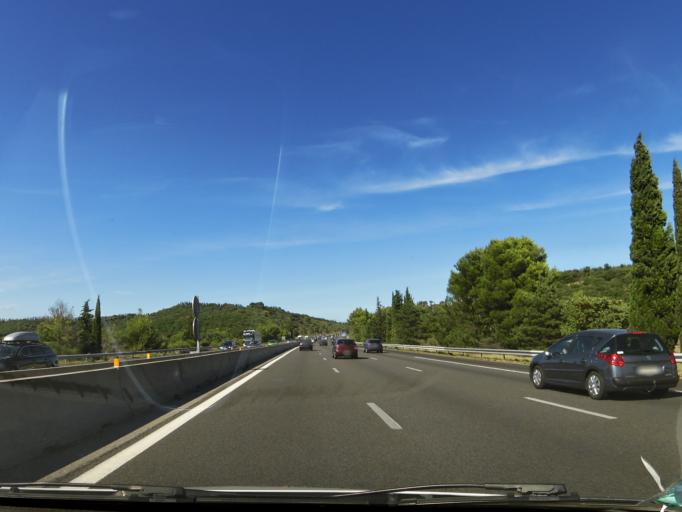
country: FR
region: Rhone-Alpes
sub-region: Departement de la Drome
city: Donzere
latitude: 44.4210
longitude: 4.7345
